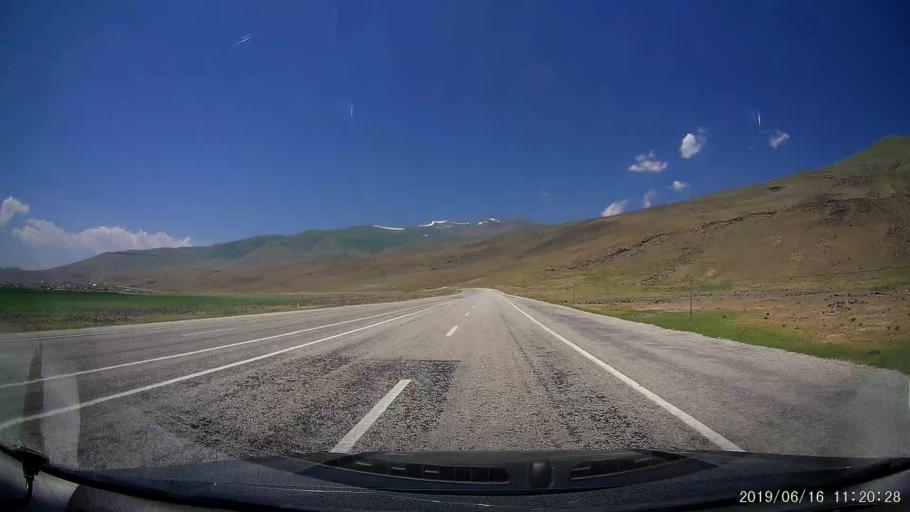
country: TR
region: Agri
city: Dogubayazit
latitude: 39.6991
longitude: 44.0897
